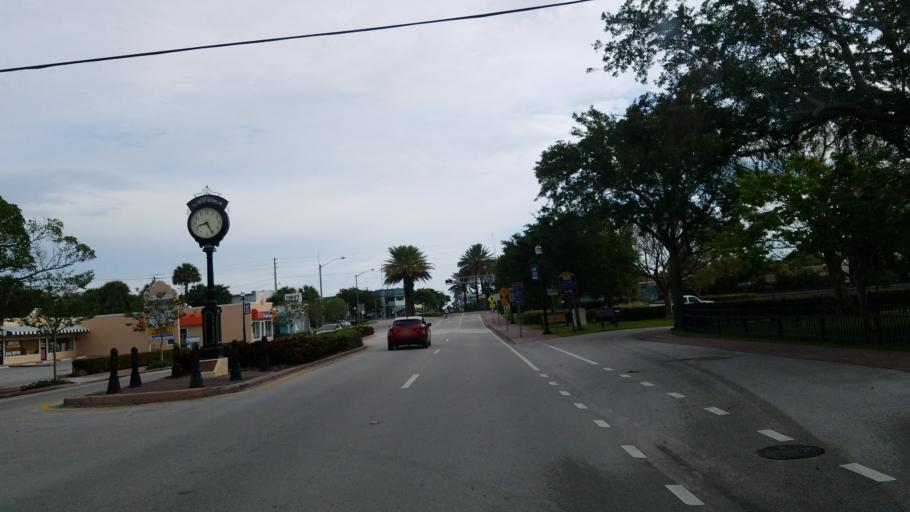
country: US
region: Florida
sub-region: Martin County
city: Stuart
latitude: 27.1962
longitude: -80.2528
